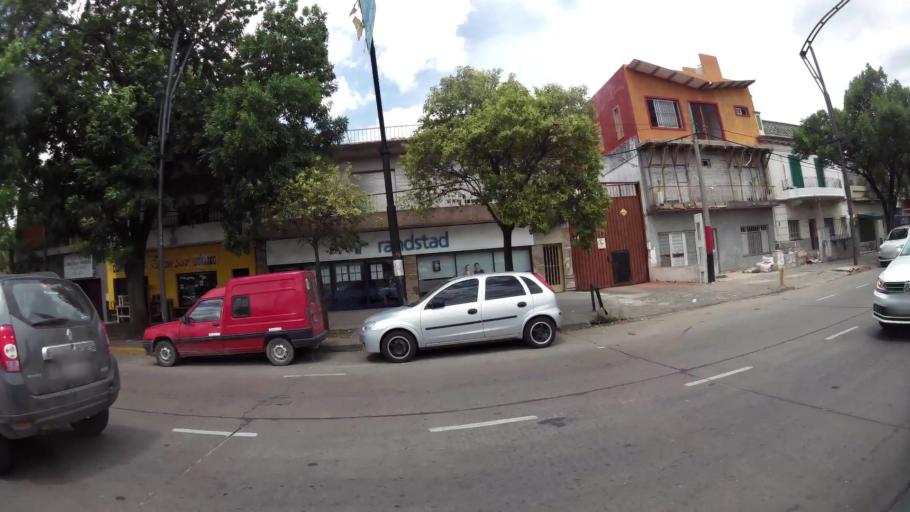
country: AR
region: Santa Fe
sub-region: Departamento de Rosario
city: Rosario
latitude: -32.9769
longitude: -60.6616
